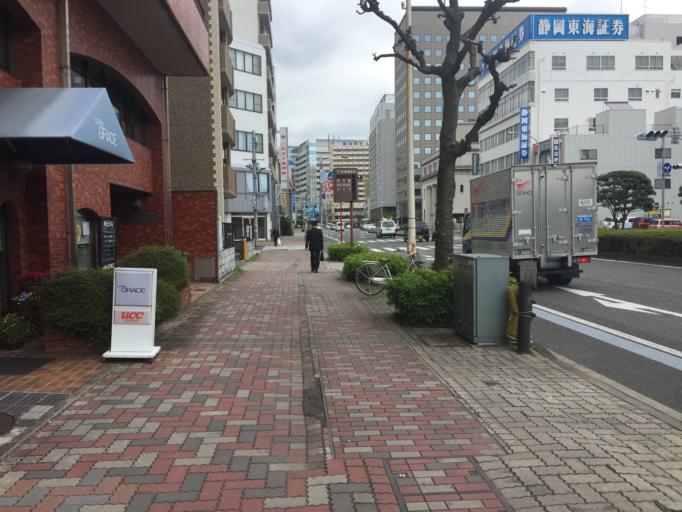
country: JP
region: Shizuoka
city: Shizuoka-shi
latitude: 34.9751
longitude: 138.3779
